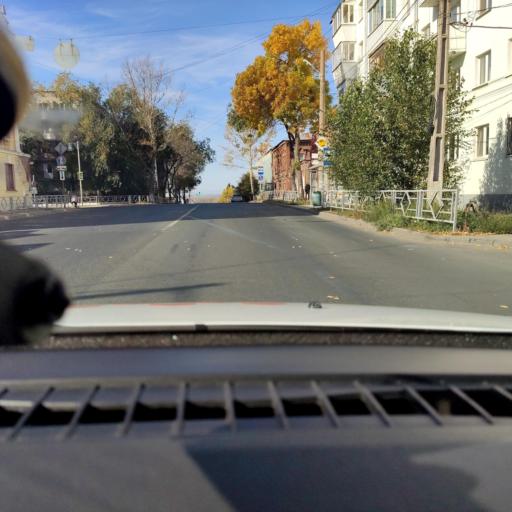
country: RU
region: Samara
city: Rozhdestveno
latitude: 53.1815
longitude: 50.0825
